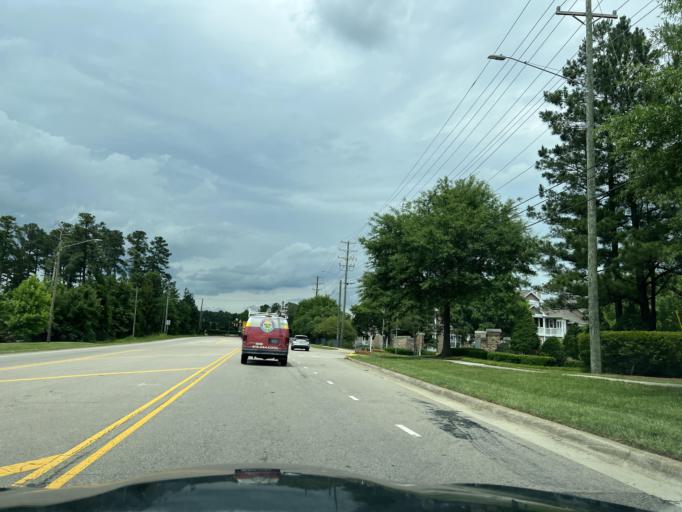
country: US
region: North Carolina
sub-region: Wake County
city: Morrisville
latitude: 35.9172
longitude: -78.8145
